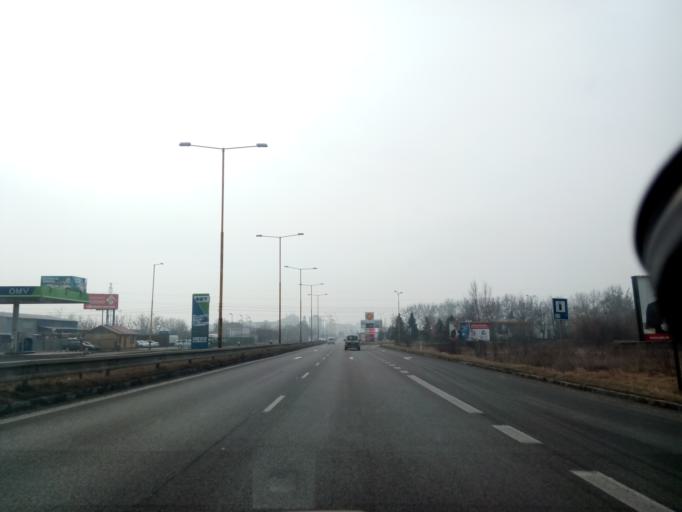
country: SK
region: Kosicky
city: Kosice
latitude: 48.7053
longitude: 21.2795
